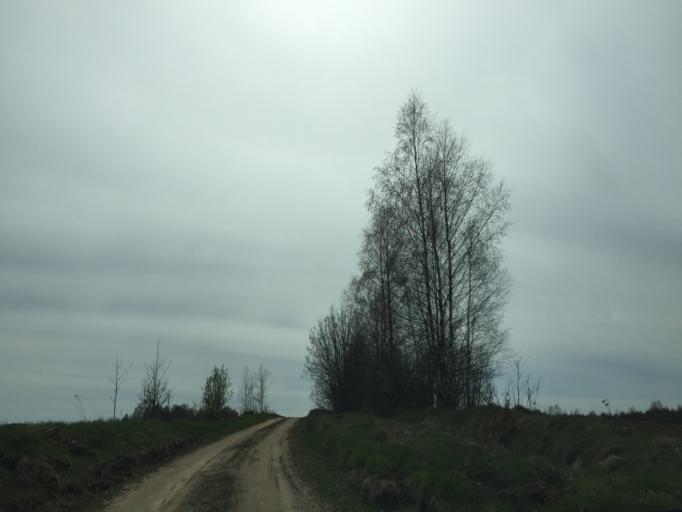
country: LV
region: Ludzas Rajons
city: Ludza
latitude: 56.5273
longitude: 27.5830
